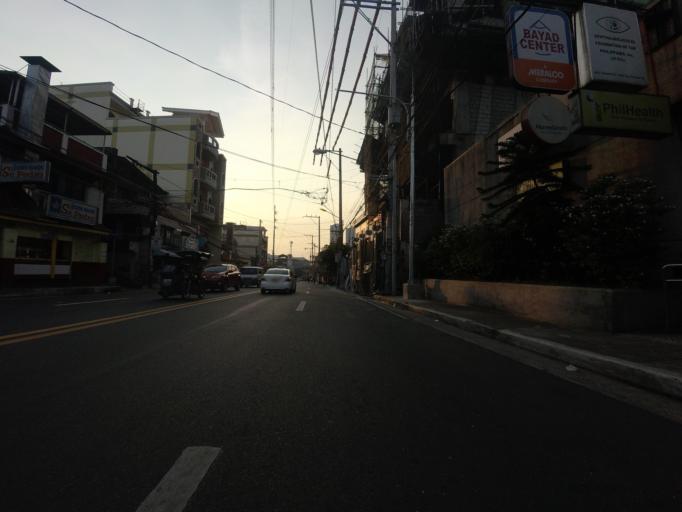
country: PH
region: Metro Manila
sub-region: San Juan
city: San Juan
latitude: 14.6039
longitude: 121.0253
